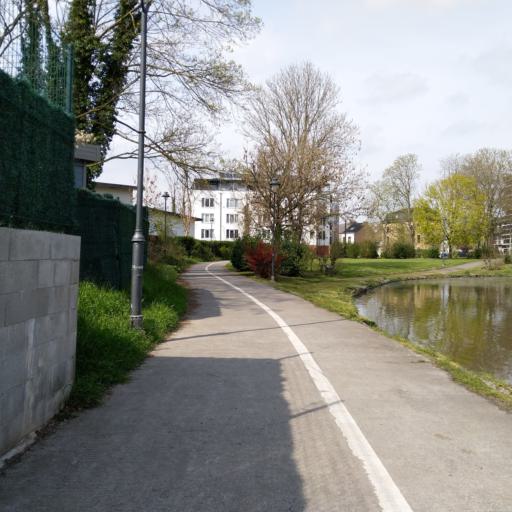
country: BE
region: Wallonia
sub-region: Province du Hainaut
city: Mons
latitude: 50.4473
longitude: 3.9621
